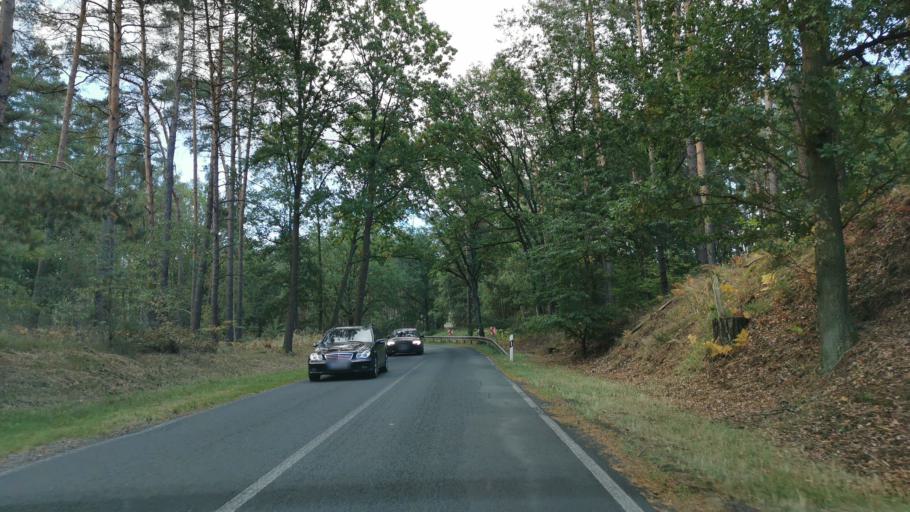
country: DE
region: Brandenburg
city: Fichtenwalde
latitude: 52.2988
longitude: 12.9445
